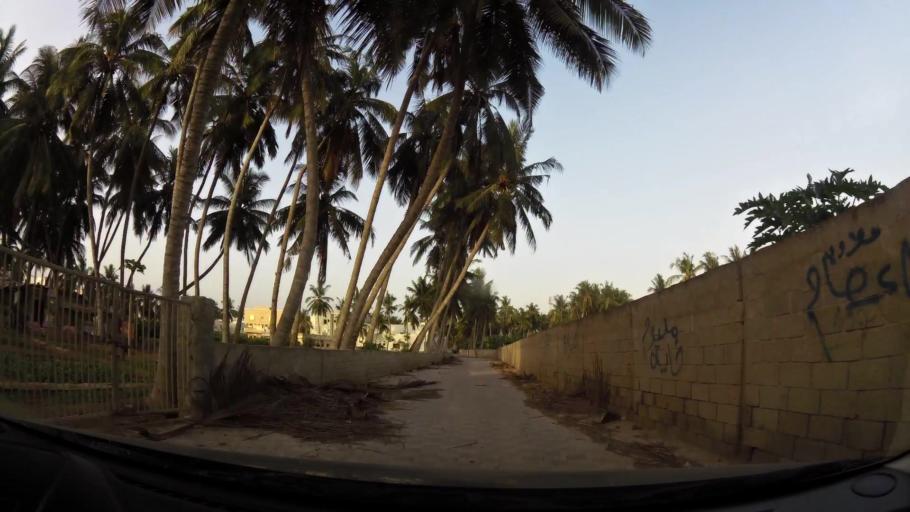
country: OM
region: Zufar
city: Salalah
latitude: 17.0142
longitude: 54.1148
